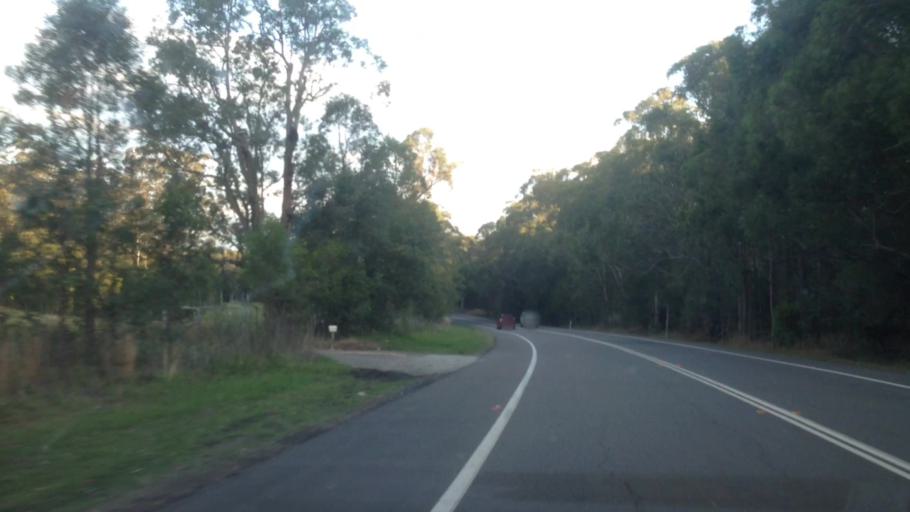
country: AU
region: New South Wales
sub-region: Lake Macquarie Shire
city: Dora Creek
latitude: -32.9924
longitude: 151.4896
